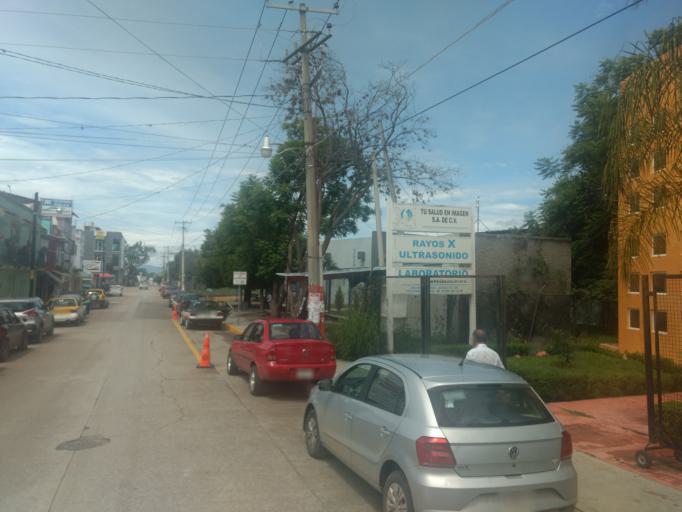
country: MX
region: Oaxaca
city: Ciudad de Huajuapam de Leon
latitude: 17.8016
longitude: -97.7794
